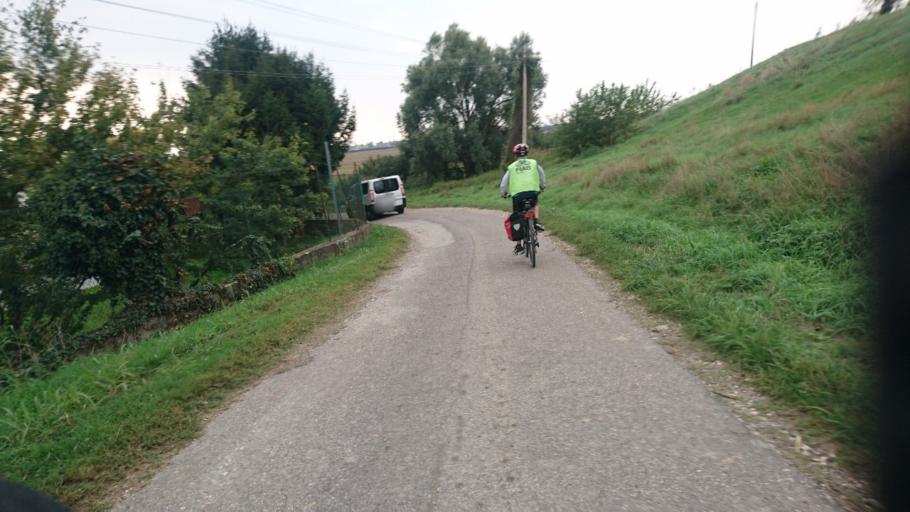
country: IT
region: Veneto
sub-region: Provincia di Verona
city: San Martino Buon Albergo
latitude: 45.4060
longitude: 11.1077
